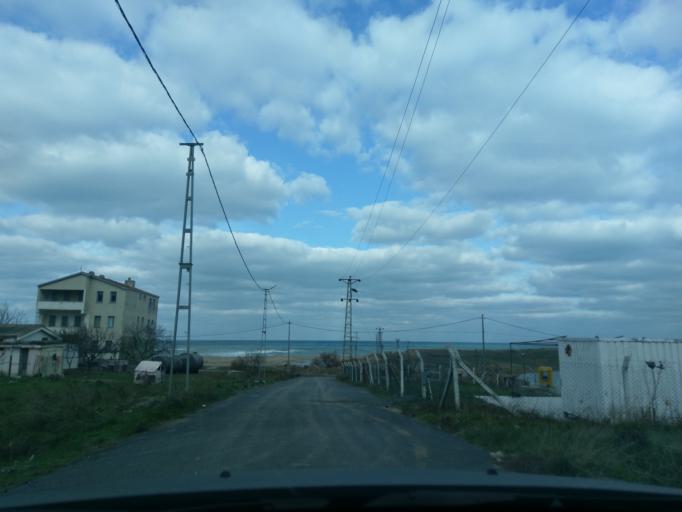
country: TR
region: Istanbul
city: Durusu
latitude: 41.3226
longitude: 28.7315
